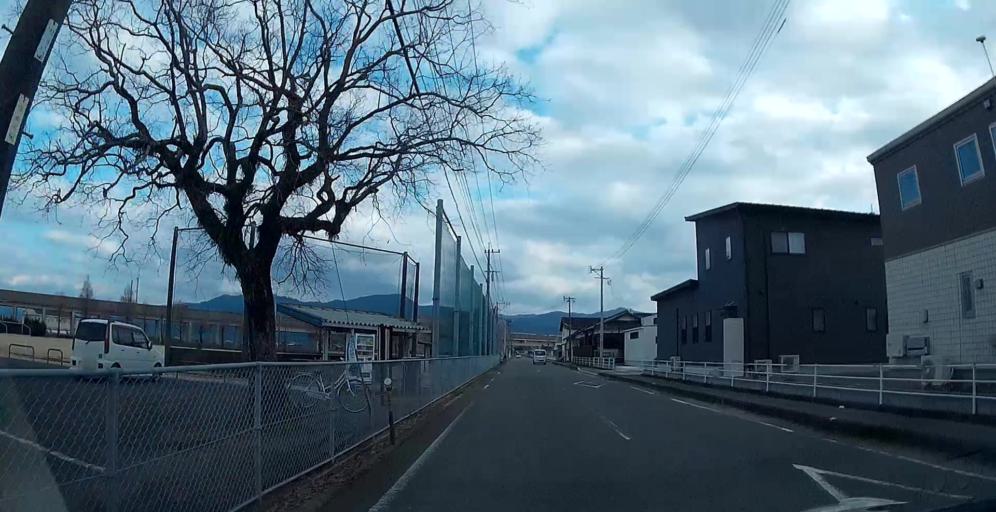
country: JP
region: Kumamoto
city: Yatsushiro
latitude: 32.5419
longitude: 130.6234
